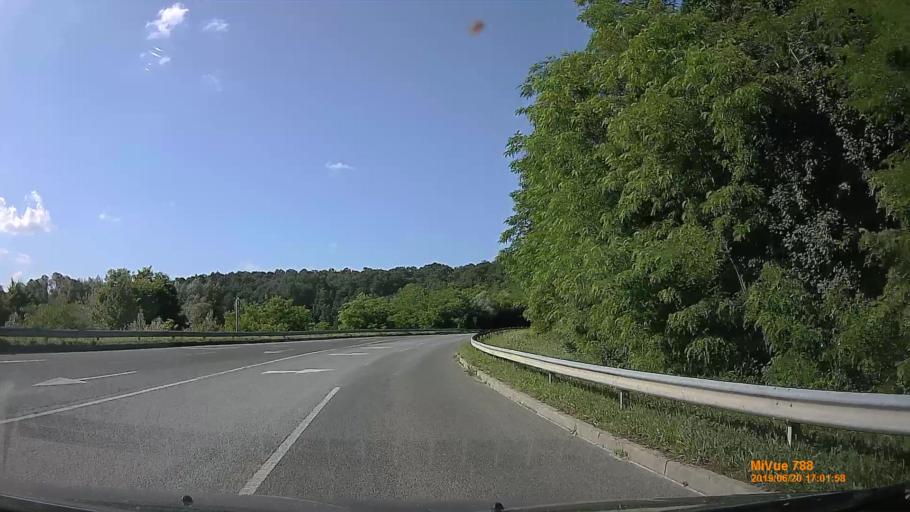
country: HU
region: Baranya
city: Buekkoesd
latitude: 46.1250
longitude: 18.0252
